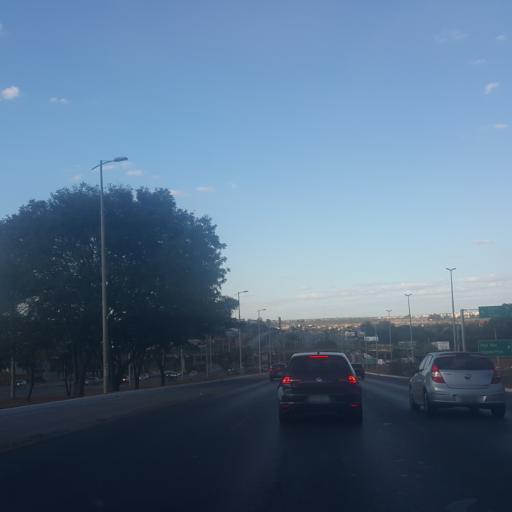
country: BR
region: Federal District
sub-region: Brasilia
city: Brasilia
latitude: -15.8237
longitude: -48.0245
